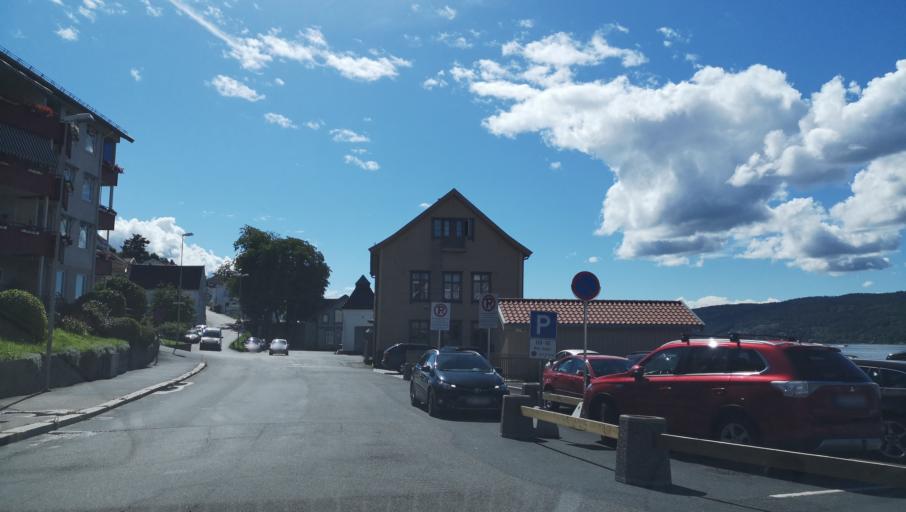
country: NO
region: Akershus
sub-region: Frogn
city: Drobak
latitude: 59.6593
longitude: 10.6302
